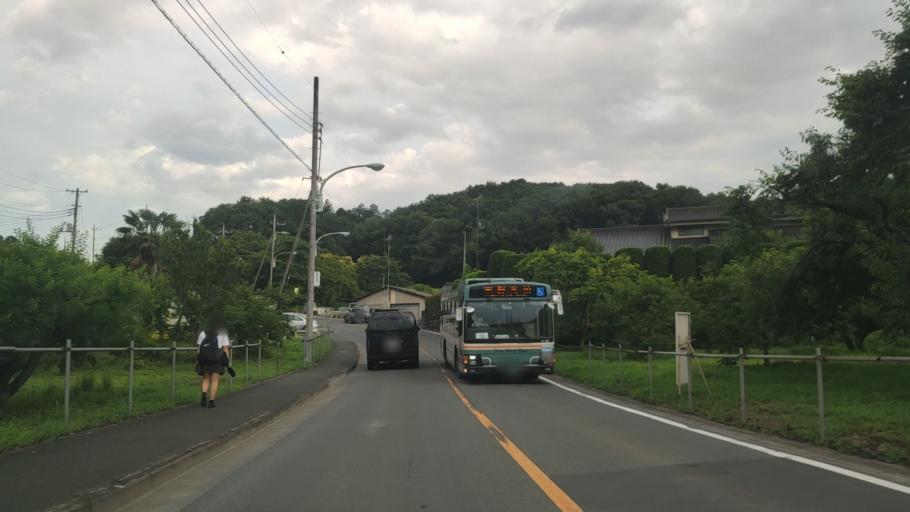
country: JP
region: Saitama
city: Hanno
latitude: 35.8232
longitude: 139.2871
